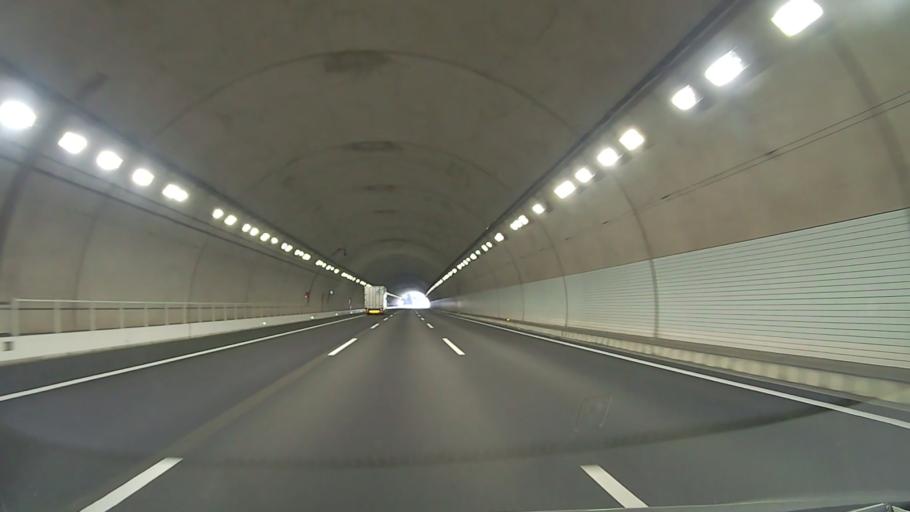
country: JP
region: Shizuoka
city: Mishima
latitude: 35.1798
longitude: 138.8871
